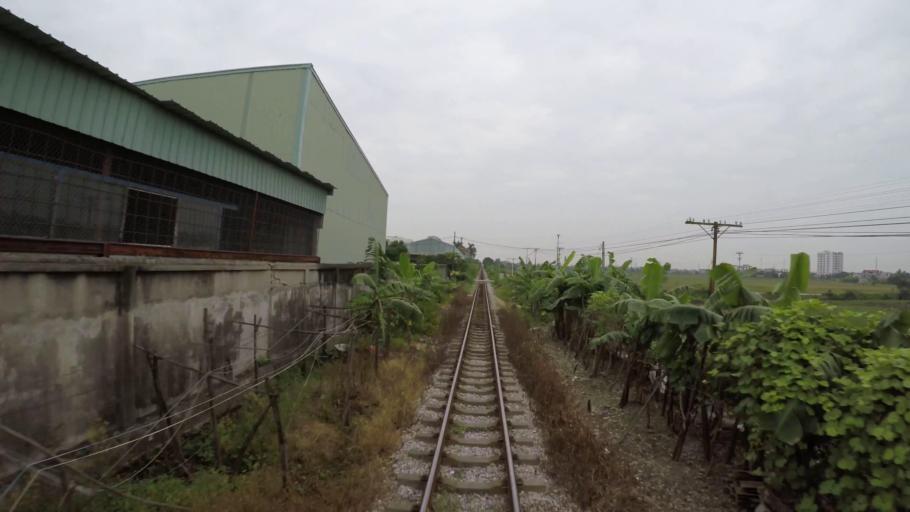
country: VN
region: Hai Phong
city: An Duong
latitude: 20.8958
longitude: 106.5856
